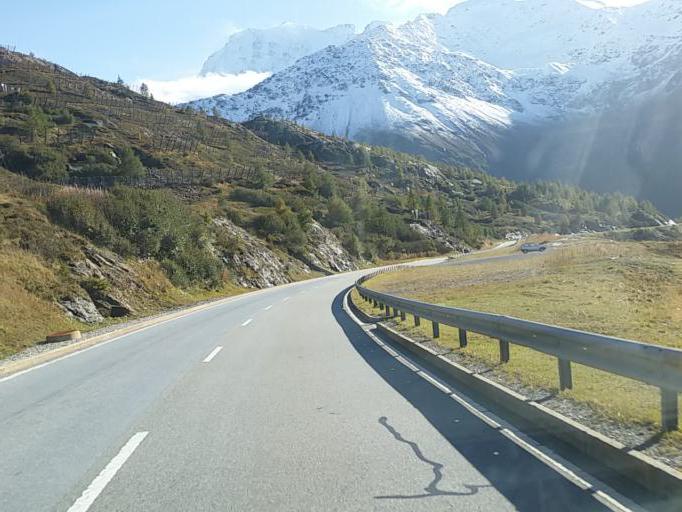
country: CH
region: Valais
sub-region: Brig District
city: Brig
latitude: 46.2394
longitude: 8.0216
